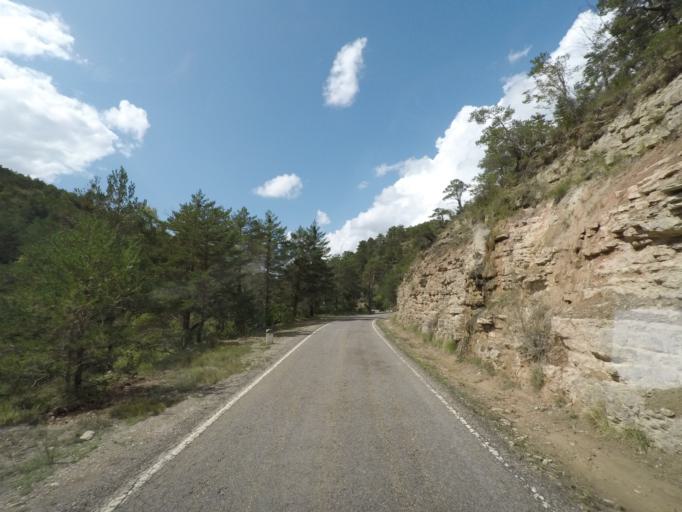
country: ES
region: Aragon
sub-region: Provincia de Huesca
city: Yebra de Basa
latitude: 42.4082
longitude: -0.2089
